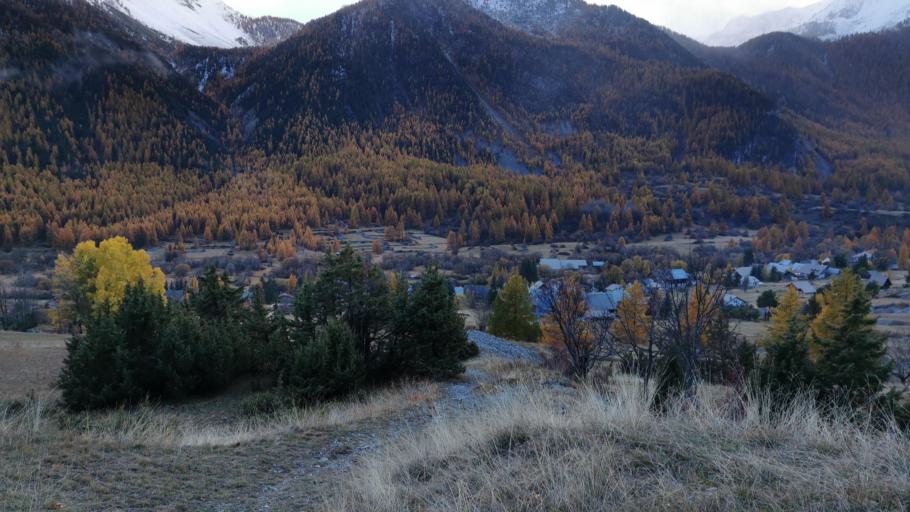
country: FR
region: Provence-Alpes-Cote d'Azur
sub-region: Departement des Hautes-Alpes
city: Villeneuve
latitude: 45.0225
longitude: 6.6195
